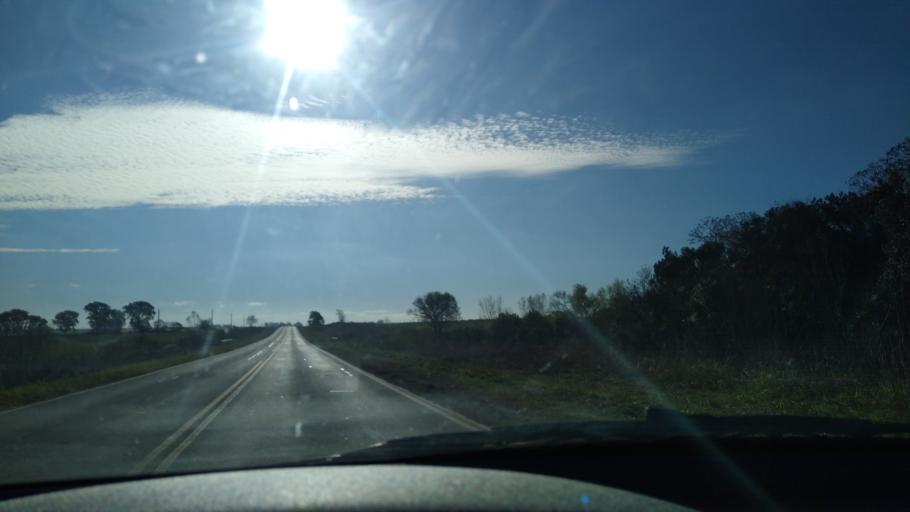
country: AR
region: Entre Rios
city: Aranguren
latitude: -32.3589
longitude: -60.3525
